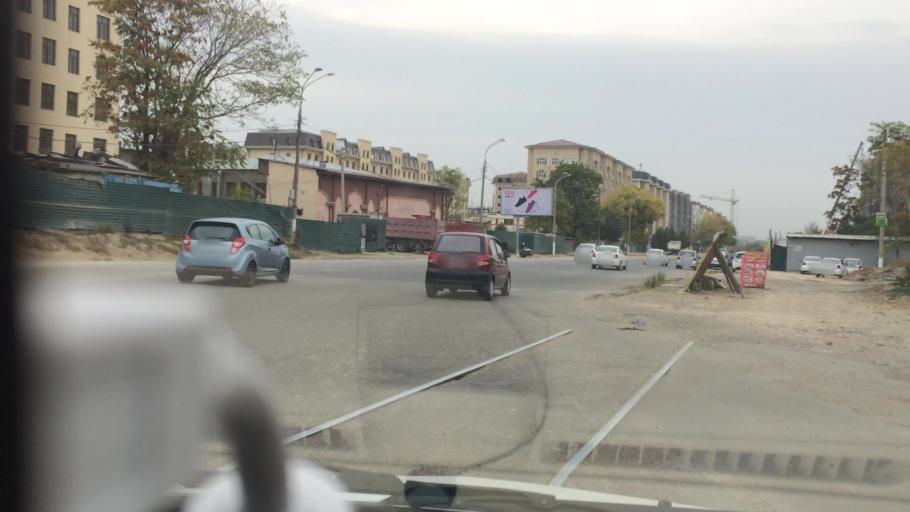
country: UZ
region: Toshkent
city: Salor
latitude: 41.3121
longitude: 69.3323
